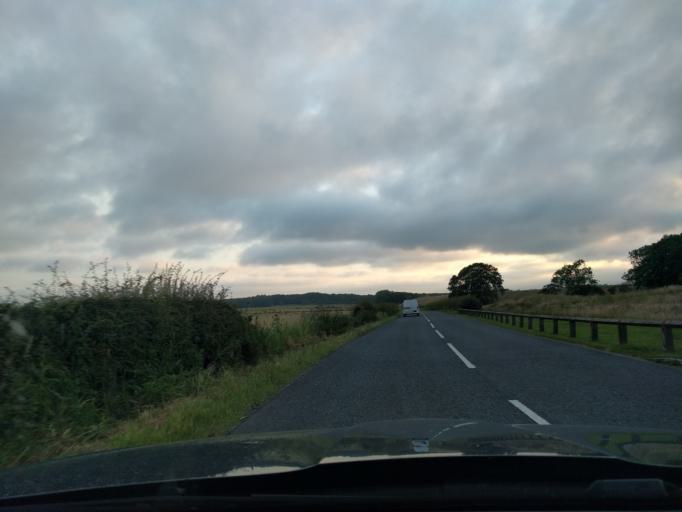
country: GB
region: England
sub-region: Northumberland
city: Cramlington
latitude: 55.0851
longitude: -1.6301
